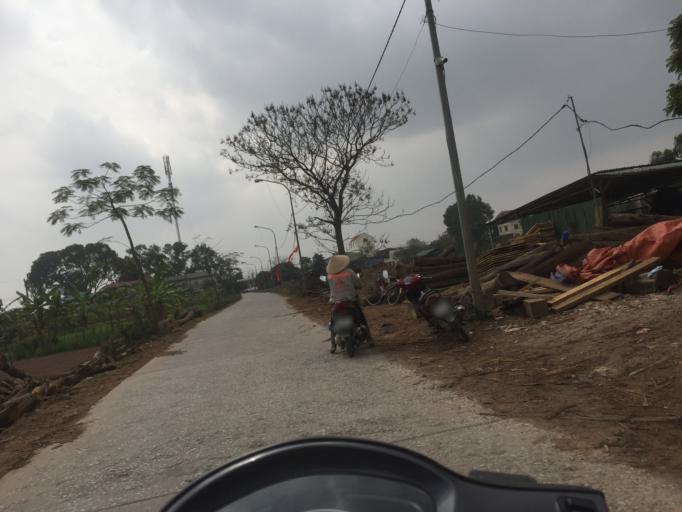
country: VN
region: Ha Noi
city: Chuc Son
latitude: 20.9064
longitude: 105.7170
